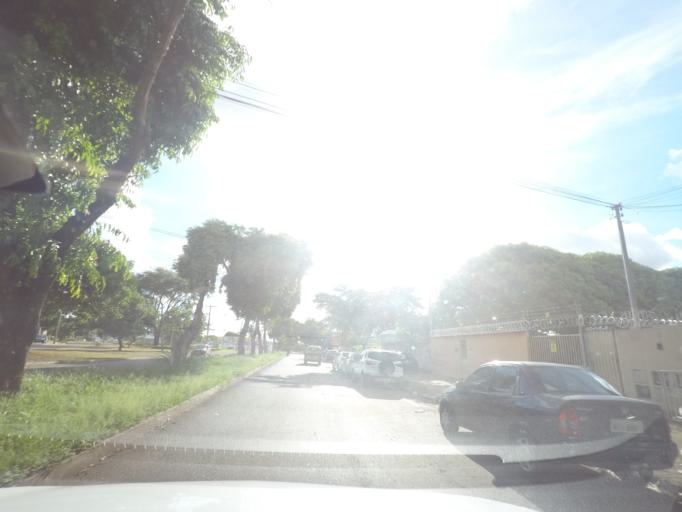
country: BR
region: Goias
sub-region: Goiania
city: Goiania
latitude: -16.7165
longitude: -49.3088
